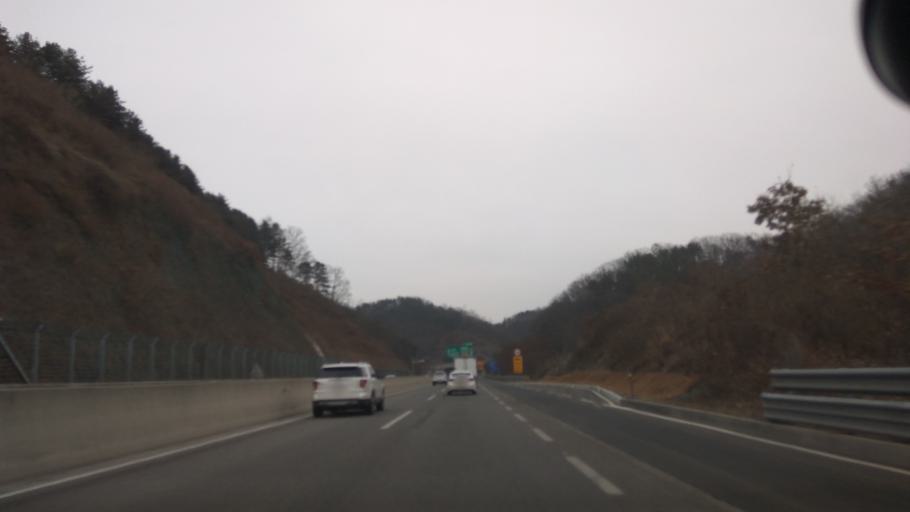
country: KR
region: Gangwon-do
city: Sindong
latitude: 37.7452
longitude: 127.6945
